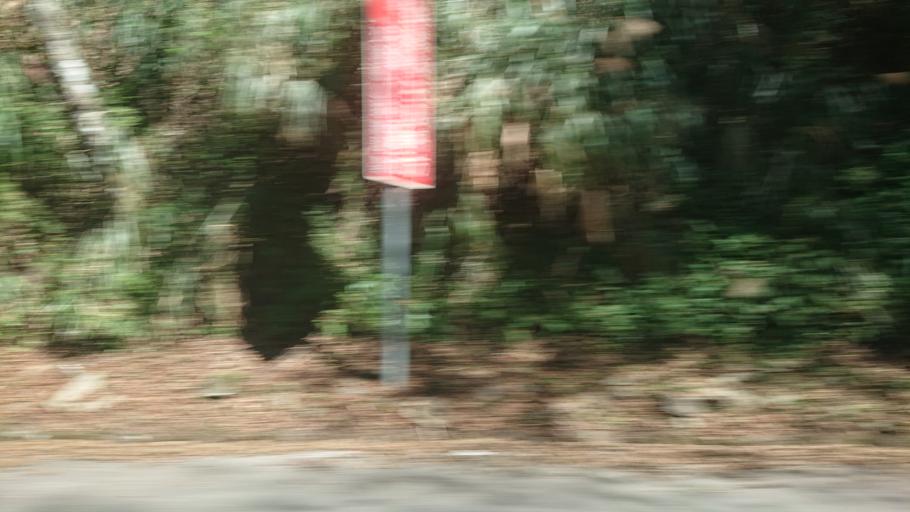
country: TW
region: Taiwan
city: Lugu
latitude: 23.4833
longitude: 120.8524
